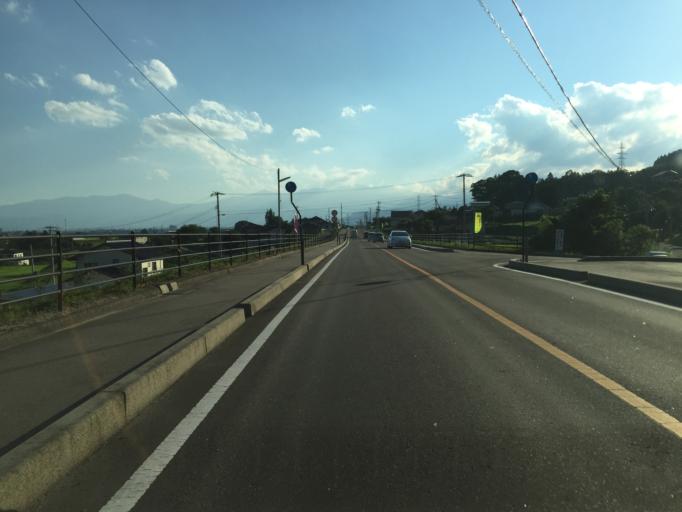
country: JP
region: Fukushima
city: Hobaramachi
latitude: 37.8340
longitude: 140.4887
